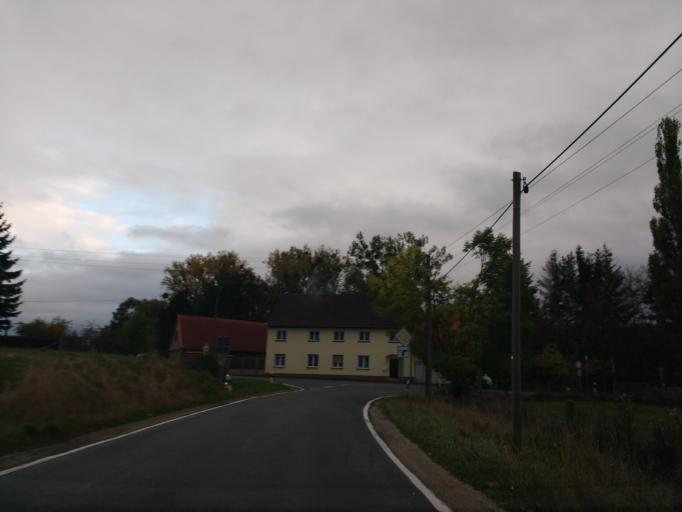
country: DE
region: Thuringia
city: Grossbodungen
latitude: 51.4805
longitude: 10.4980
